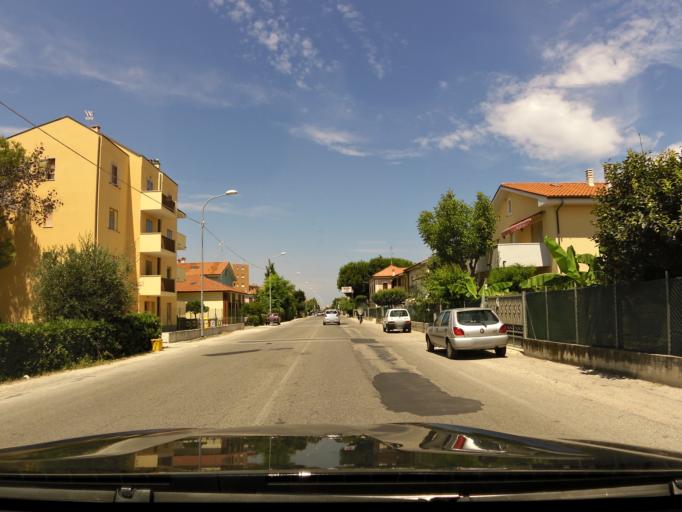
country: IT
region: The Marches
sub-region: Provincia di Ancona
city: Senigallia
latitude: 43.7324
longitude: 13.1948
